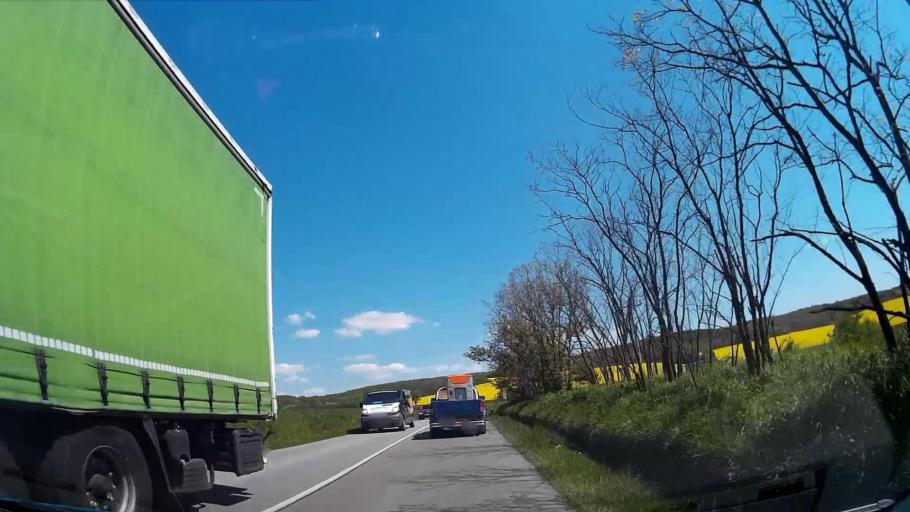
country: CZ
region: South Moravian
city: Ivancice
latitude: 49.1184
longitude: 16.3790
